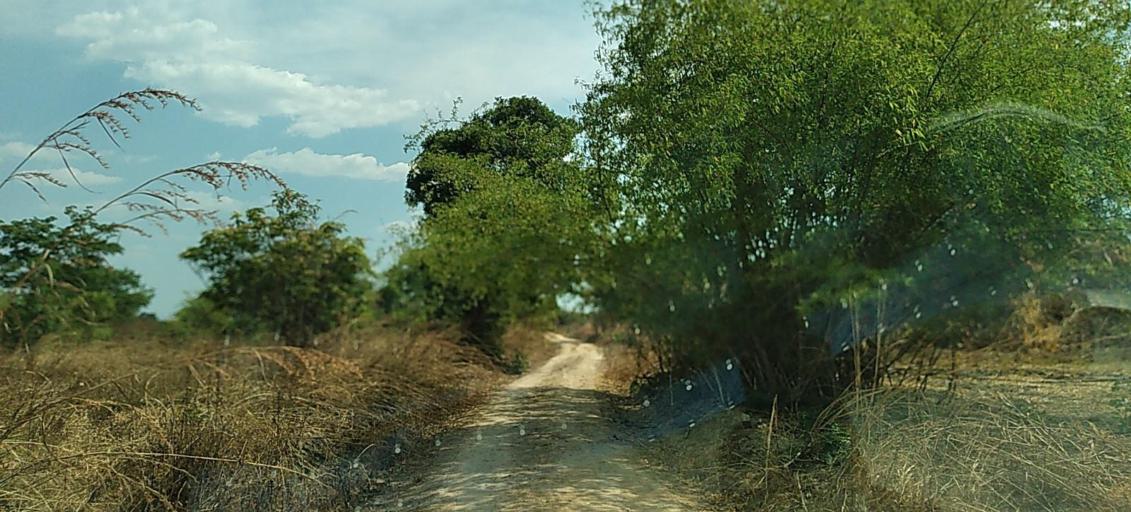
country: ZM
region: Copperbelt
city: Chililabombwe
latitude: -12.3274
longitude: 27.7872
